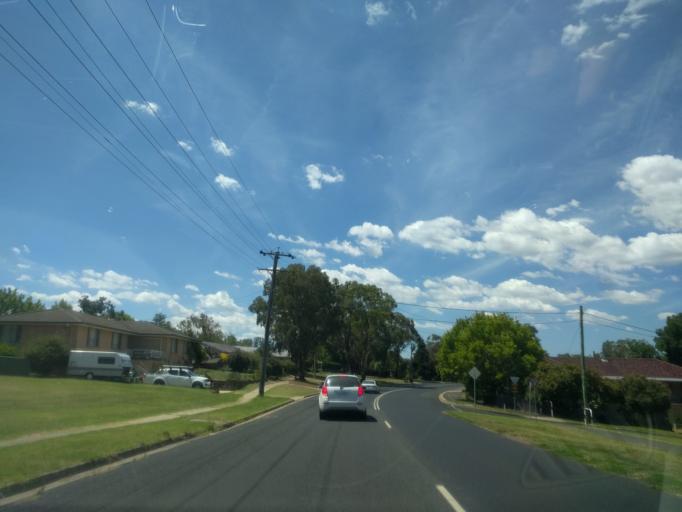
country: AU
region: New South Wales
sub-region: Armidale Dumaresq
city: Armidale
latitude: -30.5002
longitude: 151.6748
